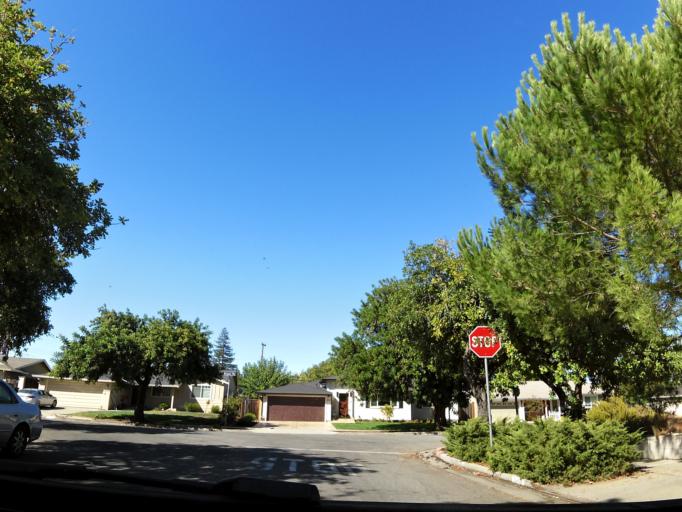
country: US
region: California
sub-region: Santa Clara County
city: Monte Sereno
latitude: 37.2689
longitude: -121.9834
